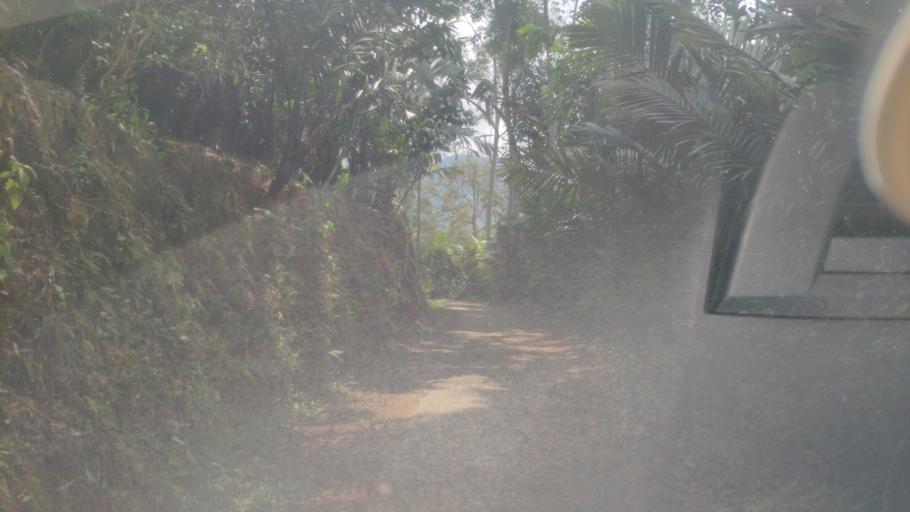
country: ID
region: Central Java
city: Wonosobo
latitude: -7.3364
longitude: 109.7865
